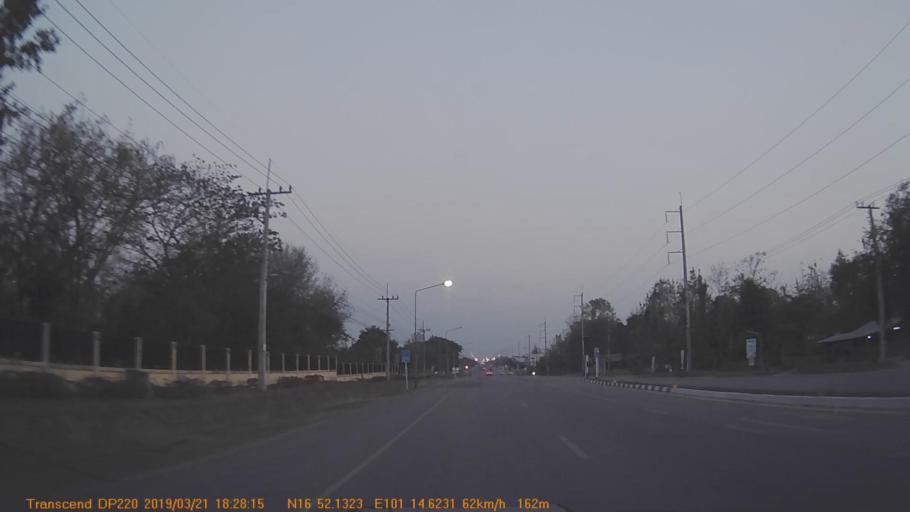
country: TH
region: Phetchabun
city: Lom Kao
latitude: 16.8687
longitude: 101.2438
